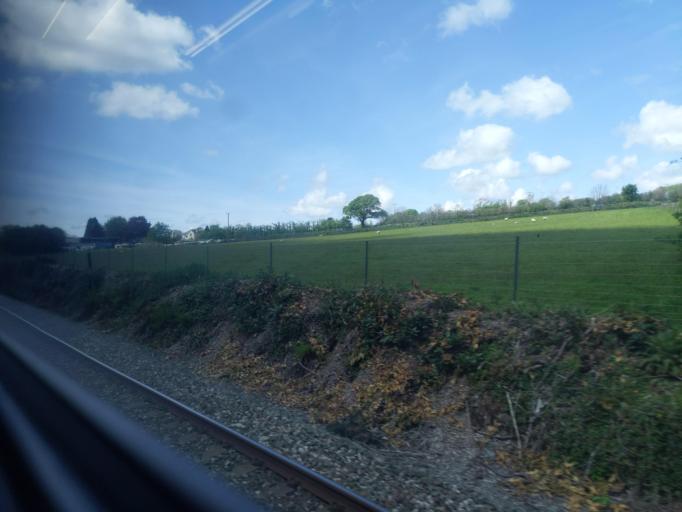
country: GB
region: England
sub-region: Cornwall
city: Liskeard
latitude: 50.4557
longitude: -4.5325
